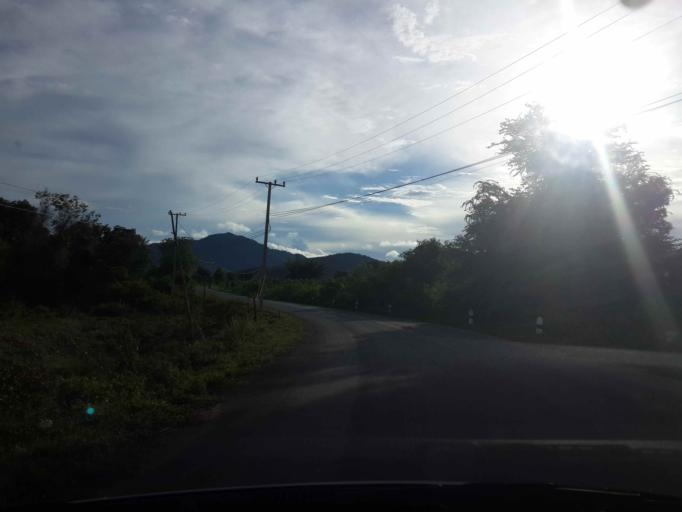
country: TH
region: Kanchanaburi
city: Dan Makham Tia
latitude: 13.8775
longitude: 99.1693
